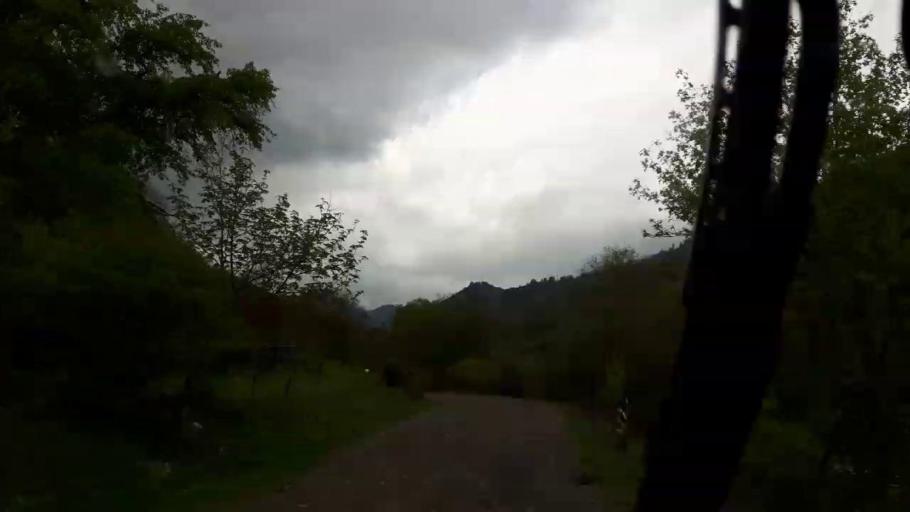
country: GE
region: Shida Kartli
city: Gori
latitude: 41.8613
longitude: 43.9459
